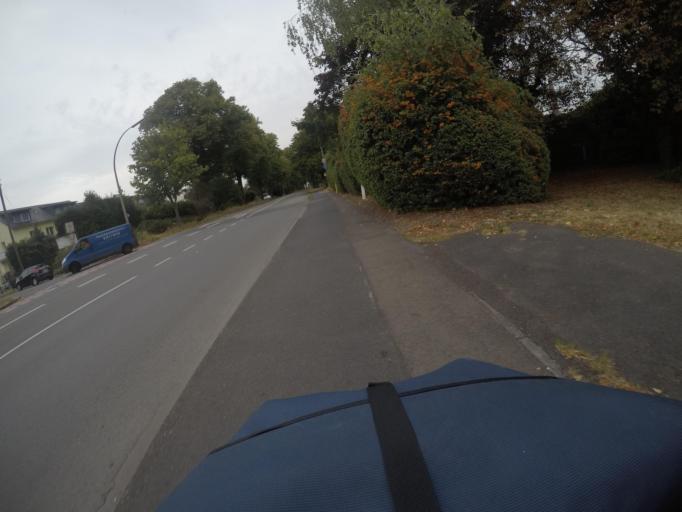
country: DE
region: North Rhine-Westphalia
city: Wesseling
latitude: 50.8540
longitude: 6.9753
